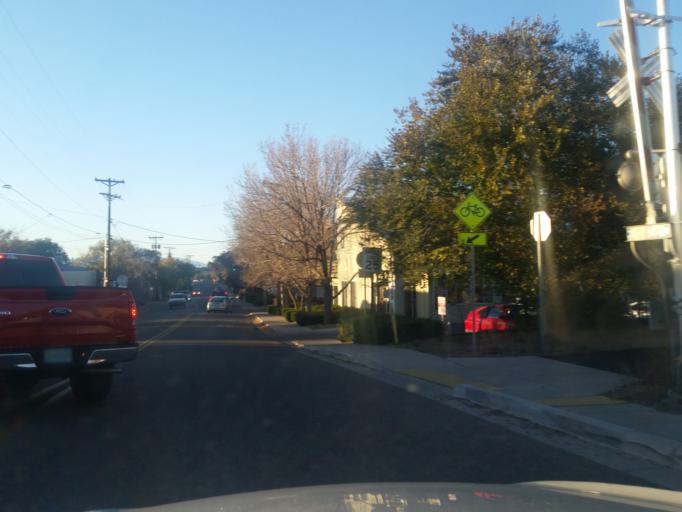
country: US
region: New Mexico
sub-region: Santa Fe County
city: Santa Fe
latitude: 35.6622
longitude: -105.9647
